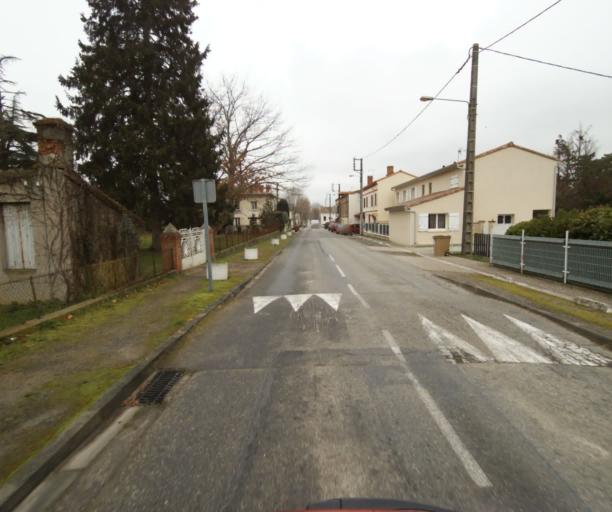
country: FR
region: Midi-Pyrenees
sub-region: Departement de la Haute-Garonne
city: Gaillac-Toulza
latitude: 43.2754
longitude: 1.5033
